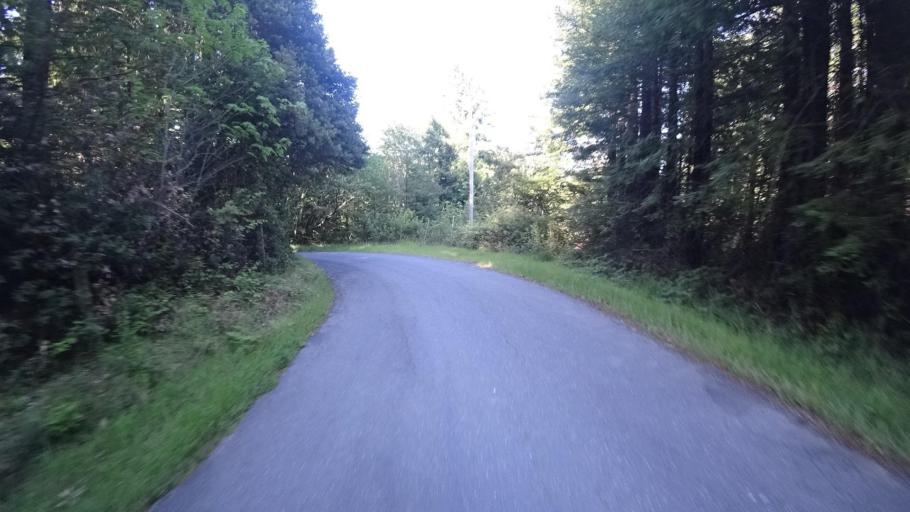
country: US
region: California
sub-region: Humboldt County
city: Rio Dell
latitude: 40.4335
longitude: -123.9689
